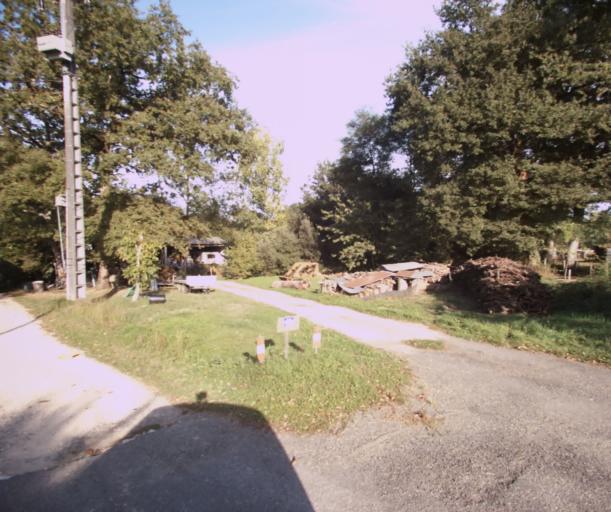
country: FR
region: Midi-Pyrenees
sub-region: Departement du Gers
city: Eauze
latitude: 43.8733
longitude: 0.0474
